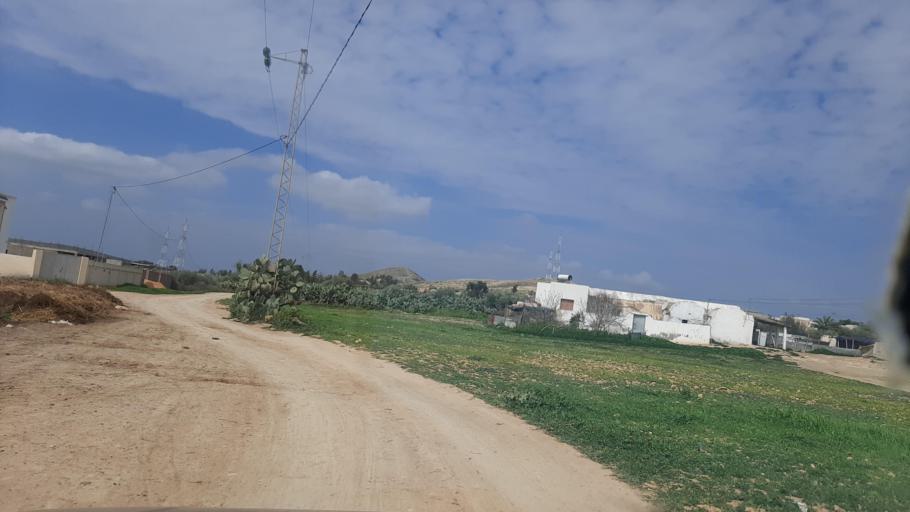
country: TN
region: Tunis
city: La Mohammedia
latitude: 36.6839
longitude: 10.0140
